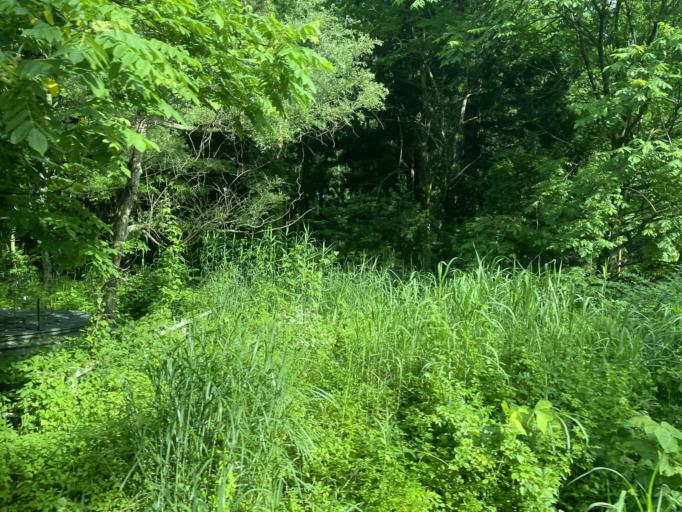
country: JP
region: Niigata
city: Suibara
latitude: 37.6909
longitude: 139.4708
